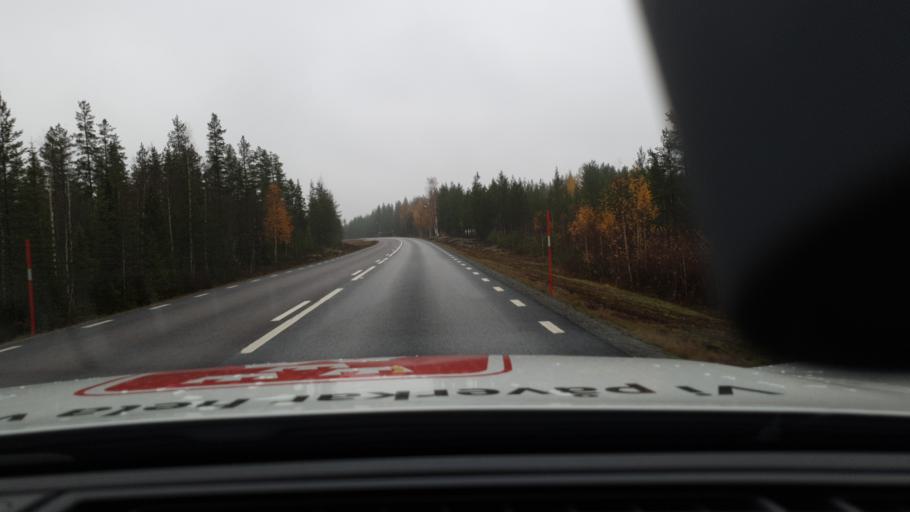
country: SE
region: Norrbotten
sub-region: Overkalix Kommun
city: OEverkalix
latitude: 66.5920
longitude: 22.2661
